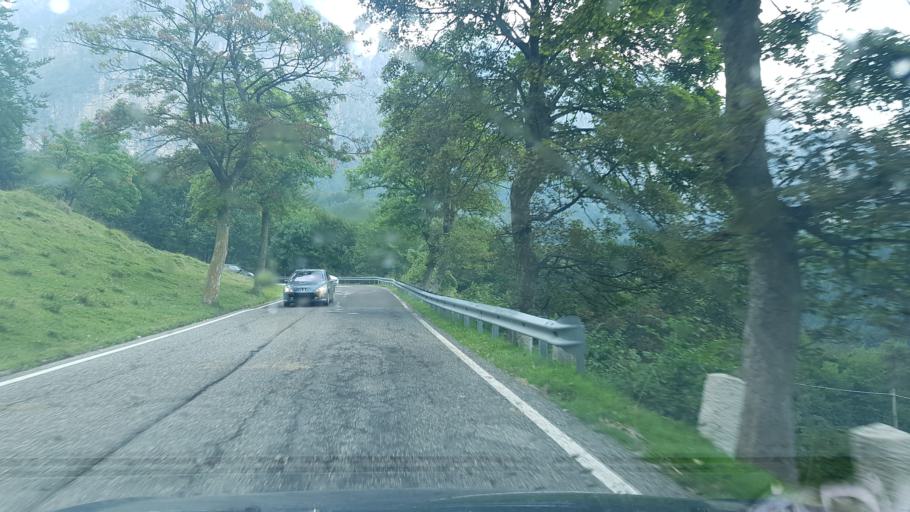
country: IT
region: Veneto
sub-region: Provincia di Vicenza
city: Recoaro Terme
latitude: 45.7613
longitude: 11.1939
